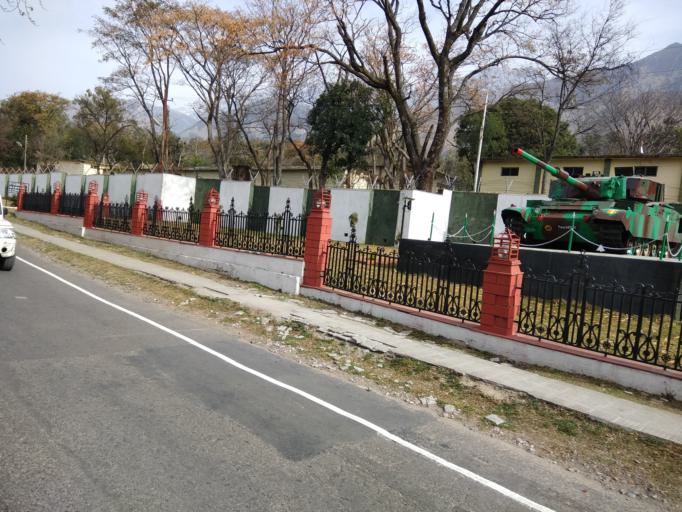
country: IN
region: Himachal Pradesh
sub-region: Kangra
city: Dharmsala
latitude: 32.1772
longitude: 76.3802
